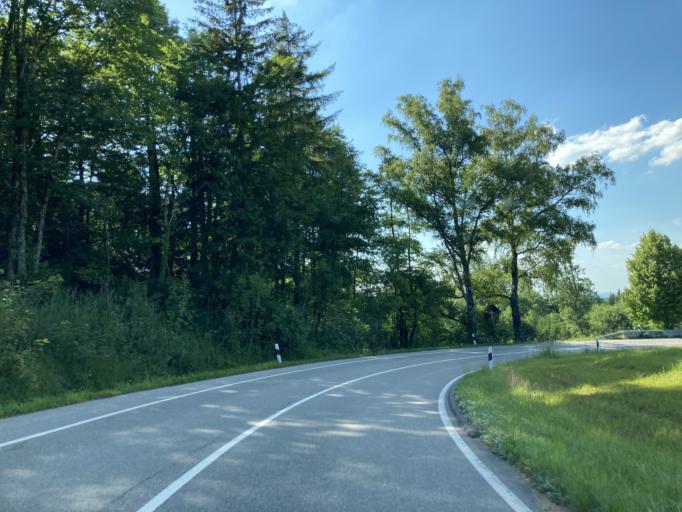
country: DE
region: Bavaria
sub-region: Upper Bavaria
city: Samerberg
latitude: 47.7850
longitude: 12.2359
